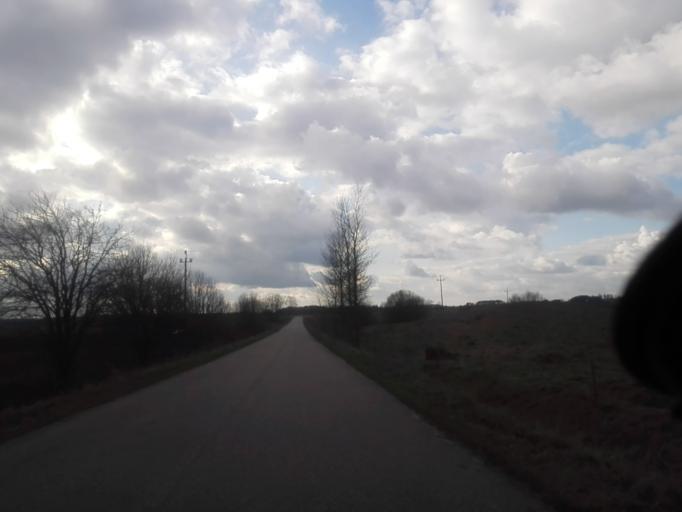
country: PL
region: Podlasie
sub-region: Suwalki
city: Suwalki
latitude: 54.2211
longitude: 22.8392
